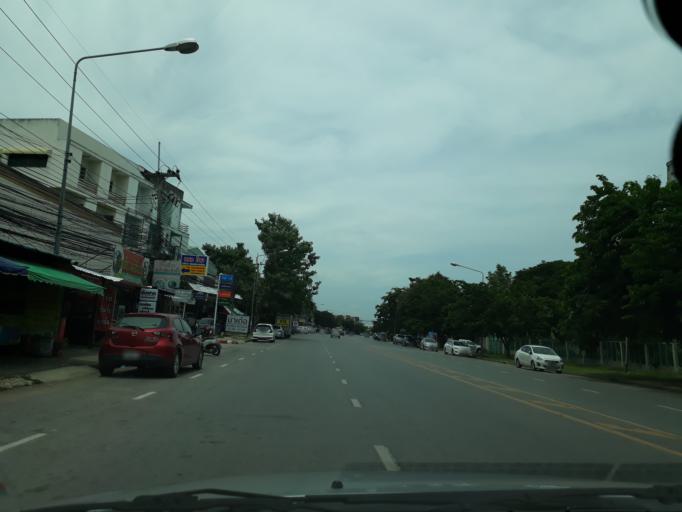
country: TH
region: Khon Kaen
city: Khon Kaen
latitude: 16.4335
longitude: 102.8644
